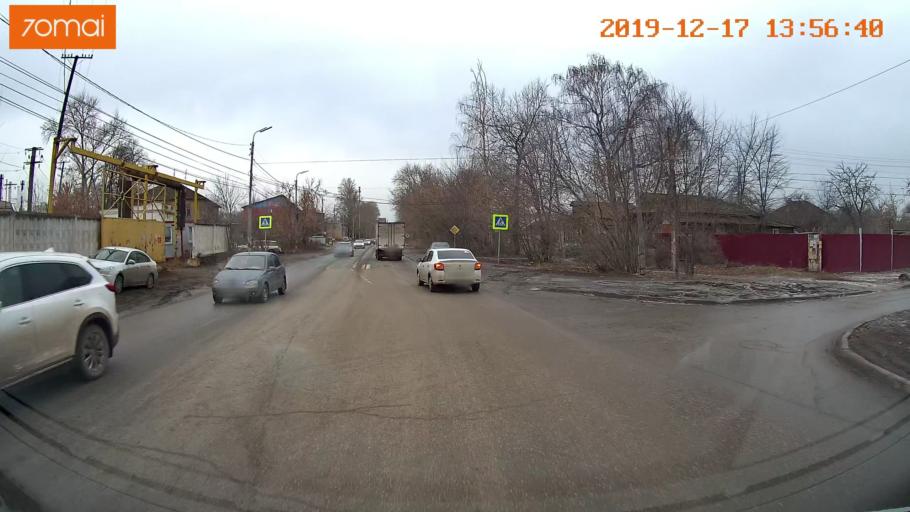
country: RU
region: Rjazan
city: Ryazan'
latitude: 54.6273
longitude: 39.6942
